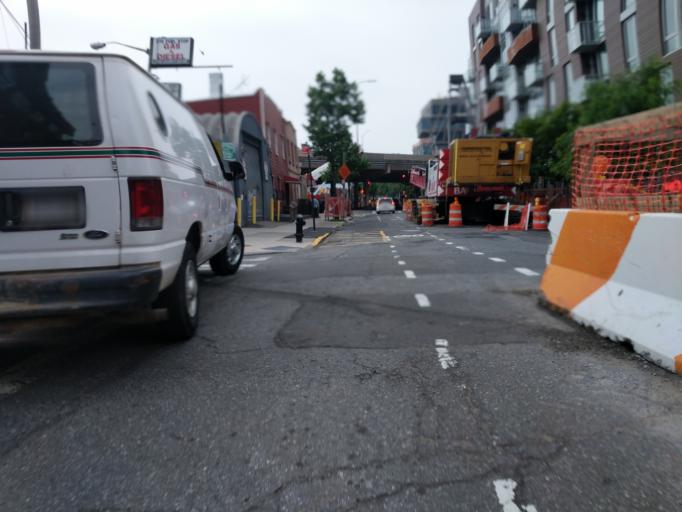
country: US
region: New York
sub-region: Queens County
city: Long Island City
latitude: 40.7186
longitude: -73.9484
